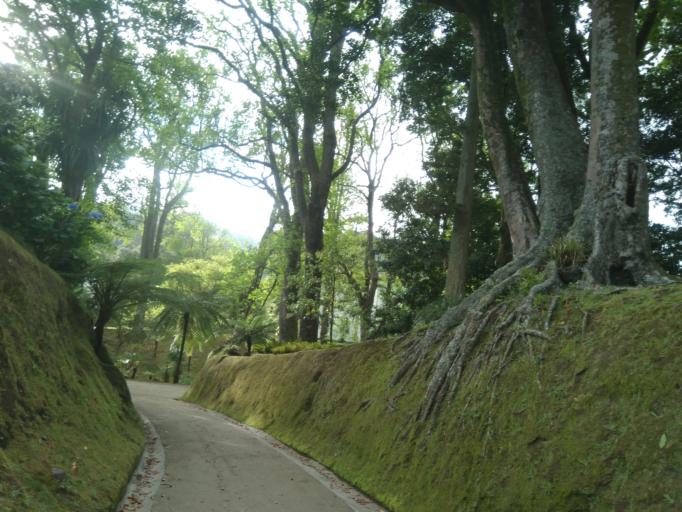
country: PT
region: Azores
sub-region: Povoacao
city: Furnas
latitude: 37.7706
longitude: -25.3140
